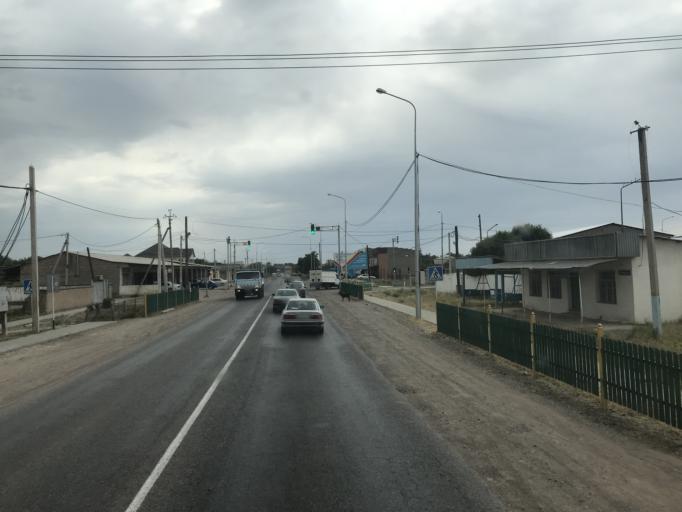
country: KZ
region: Ongtustik Qazaqstan
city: Saryaghash
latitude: 41.3482
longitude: 68.9614
